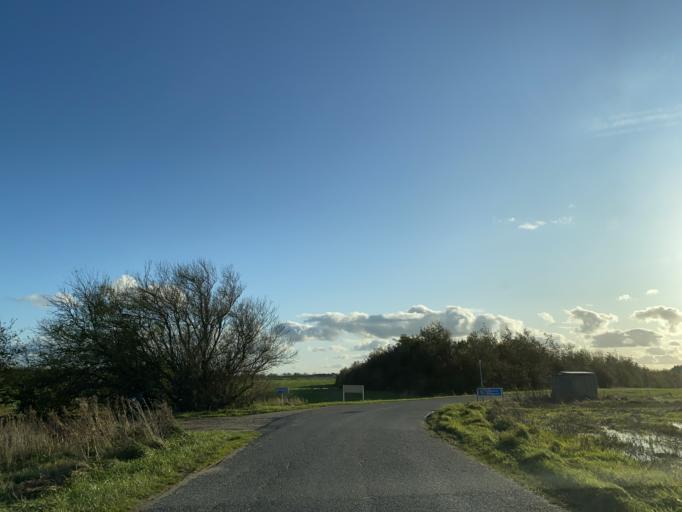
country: DK
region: Central Jutland
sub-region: Viborg Kommune
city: Bjerringbro
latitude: 56.3283
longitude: 9.7090
